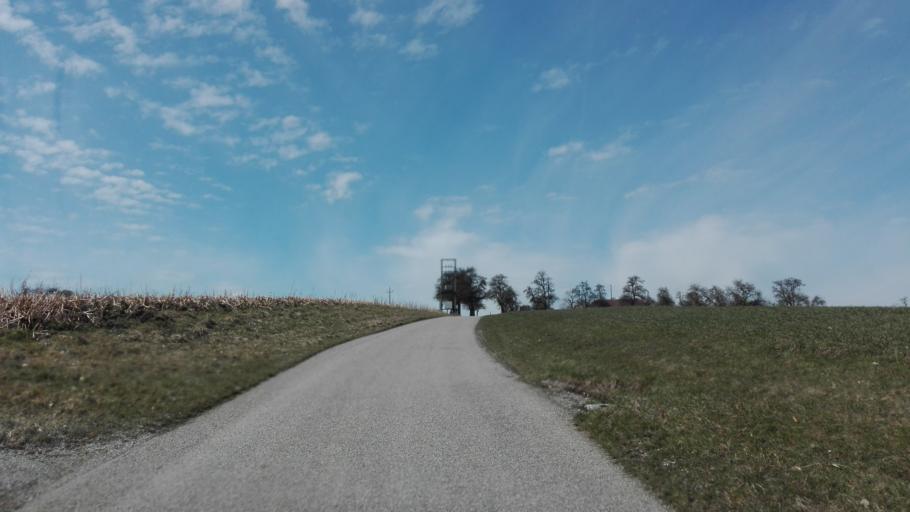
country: AT
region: Upper Austria
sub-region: Politischer Bezirk Grieskirchen
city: Grieskirchen
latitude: 48.2347
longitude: 13.8639
